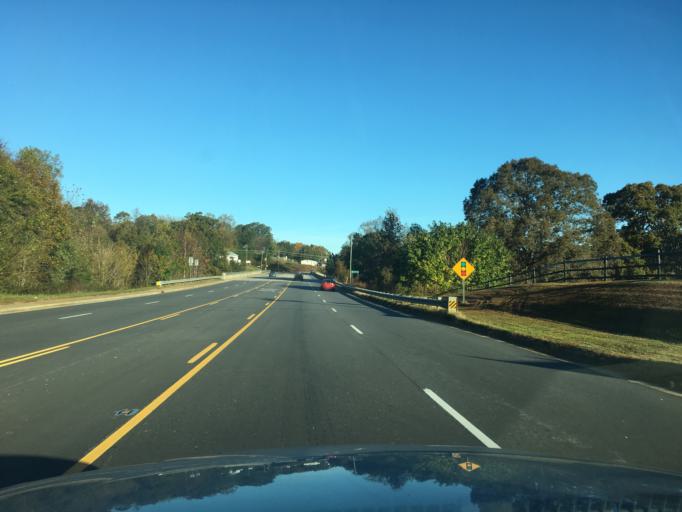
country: US
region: North Carolina
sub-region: Catawba County
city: Mountain View
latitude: 35.6997
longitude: -81.3478
